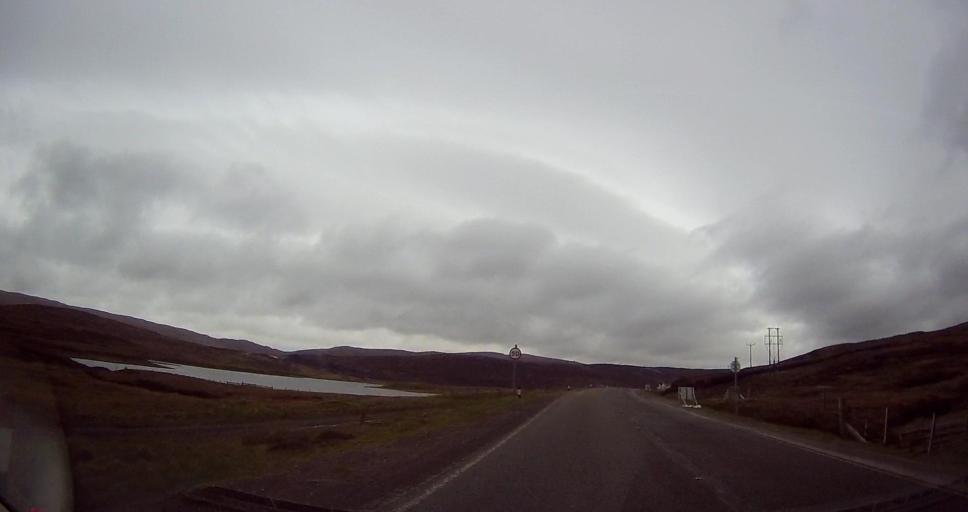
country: GB
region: Scotland
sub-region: Shetland Islands
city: Lerwick
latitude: 60.2726
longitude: -1.2395
